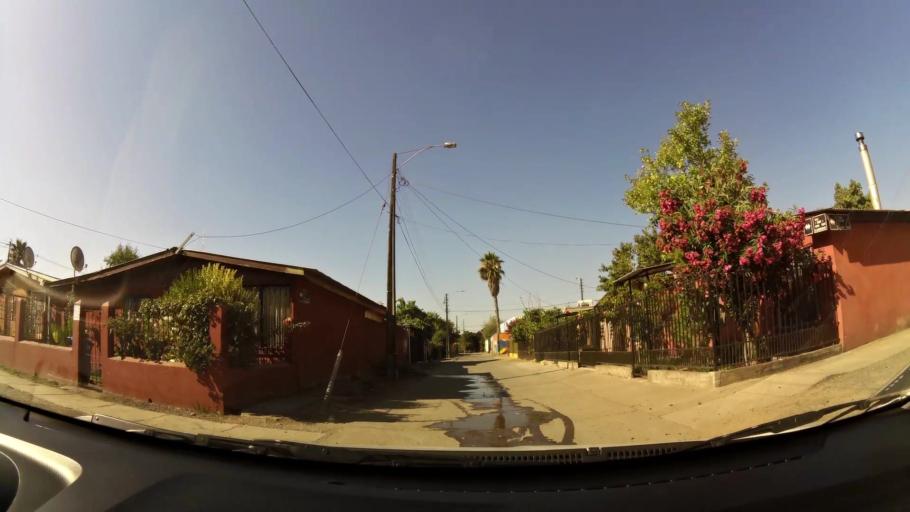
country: CL
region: Maule
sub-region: Provincia de Talca
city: Talca
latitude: -35.4469
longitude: -71.6587
